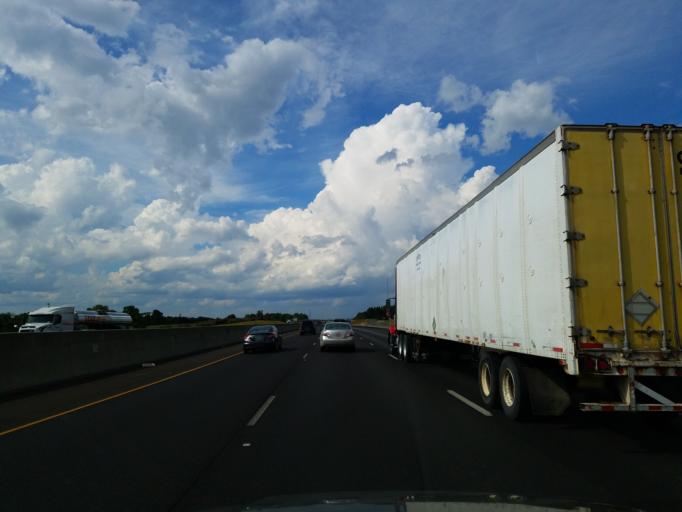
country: US
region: Georgia
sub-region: Tift County
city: Tifton
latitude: 31.5262
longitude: -83.5214
